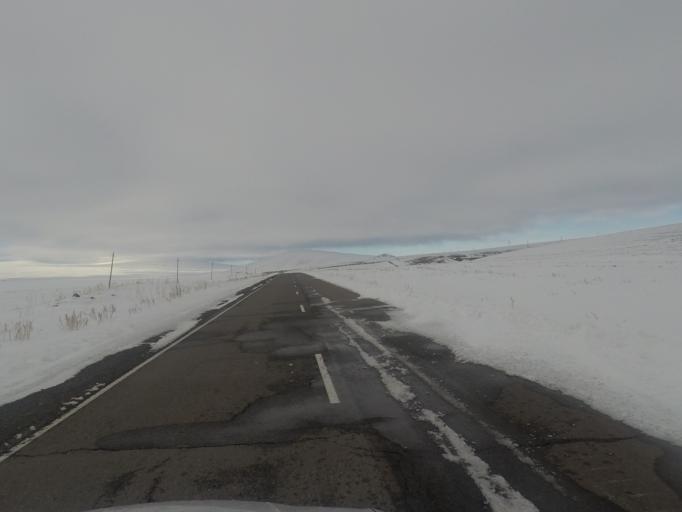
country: GE
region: Samtskhe-Javakheti
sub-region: Ninotsminda
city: Ninotsminda
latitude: 41.4260
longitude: 43.8355
